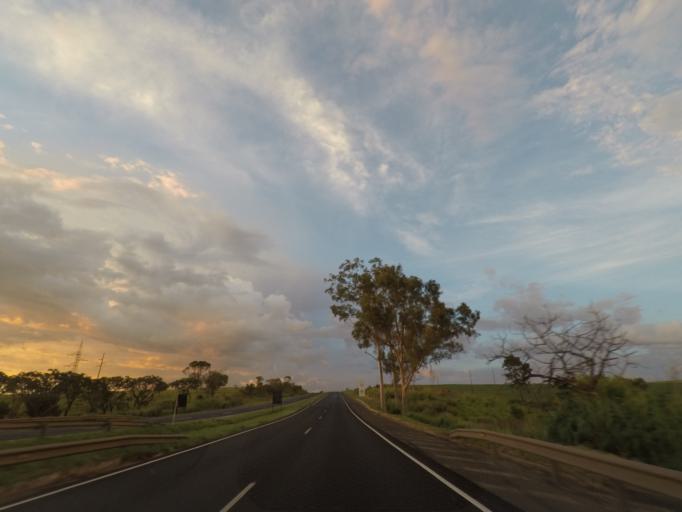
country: BR
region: Minas Gerais
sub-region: Uberaba
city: Uberaba
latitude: -19.6179
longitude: -48.0184
